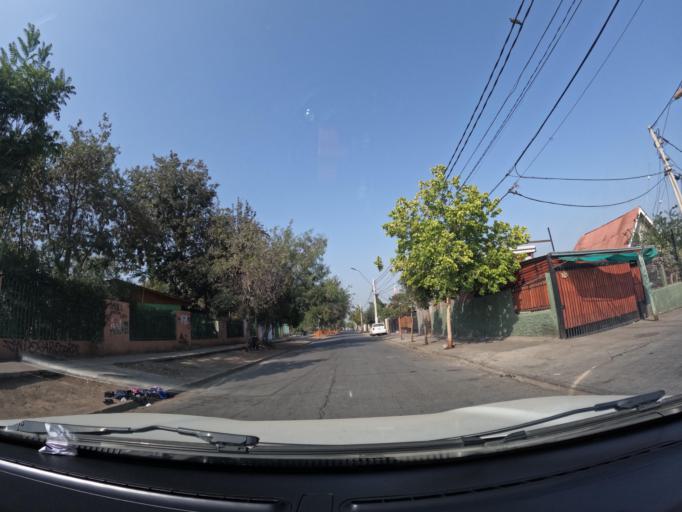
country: CL
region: Santiago Metropolitan
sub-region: Provincia de Santiago
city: Villa Presidente Frei, Nunoa, Santiago, Chile
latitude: -33.4726
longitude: -70.5699
